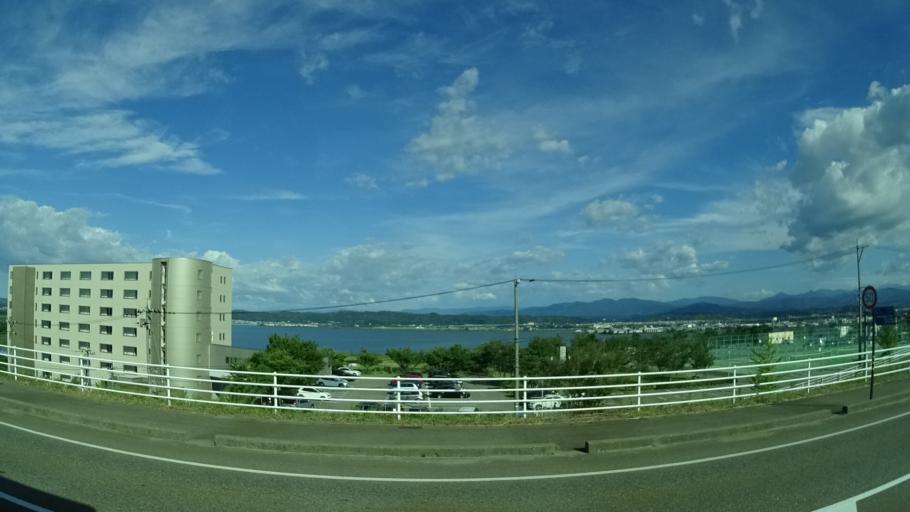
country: JP
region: Ishikawa
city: Kanazawa-shi
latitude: 36.6579
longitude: 136.6490
